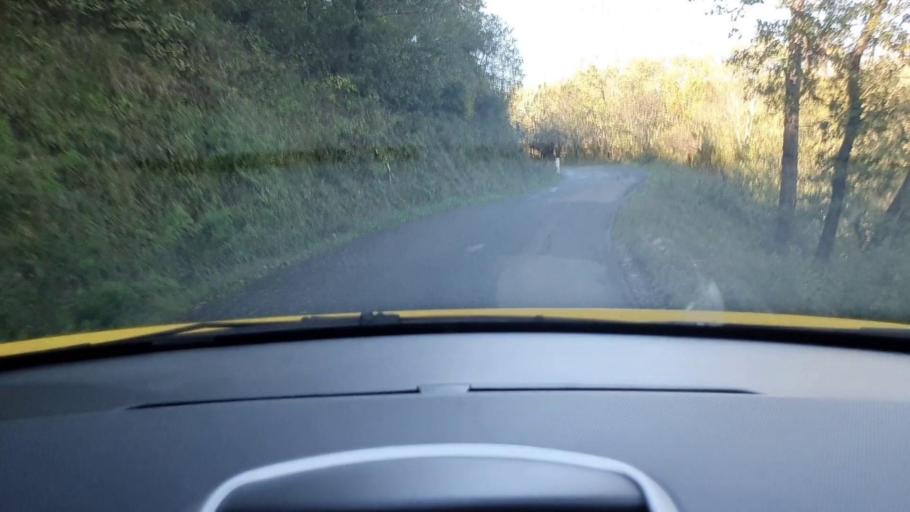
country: FR
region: Languedoc-Roussillon
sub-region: Departement du Gard
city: Saint-Hippolyte-du-Fort
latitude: 43.9704
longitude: 3.7935
